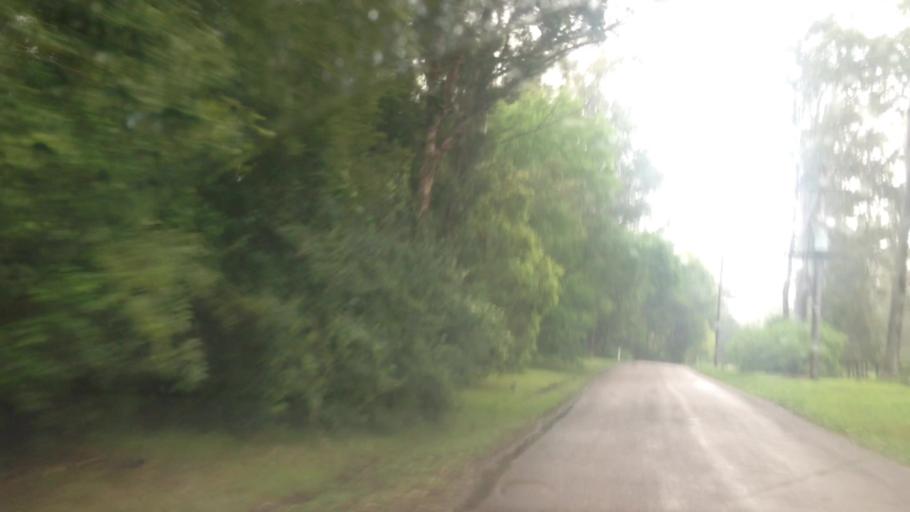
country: AU
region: New South Wales
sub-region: Wyong Shire
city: Little Jilliby
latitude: -33.1886
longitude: 151.3617
